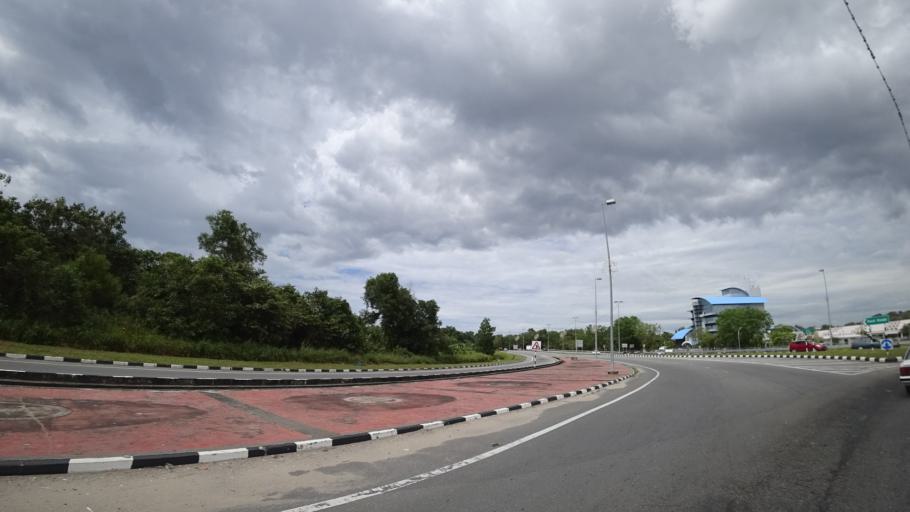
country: BN
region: Brunei and Muara
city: Bandar Seri Begawan
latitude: 4.8959
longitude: 114.9006
